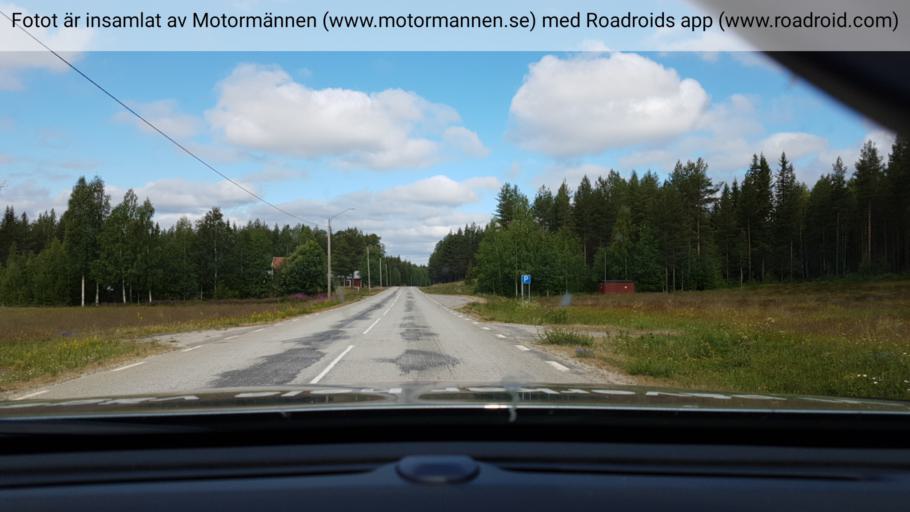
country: SE
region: Vaesterbotten
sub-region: Lycksele Kommun
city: Lycksele
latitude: 64.7687
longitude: 19.0375
